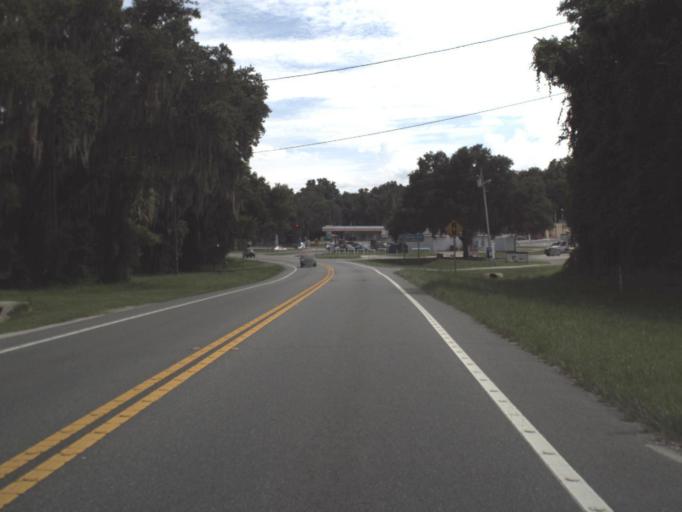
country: US
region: Florida
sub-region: Citrus County
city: Hernando
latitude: 28.9056
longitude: -82.3764
